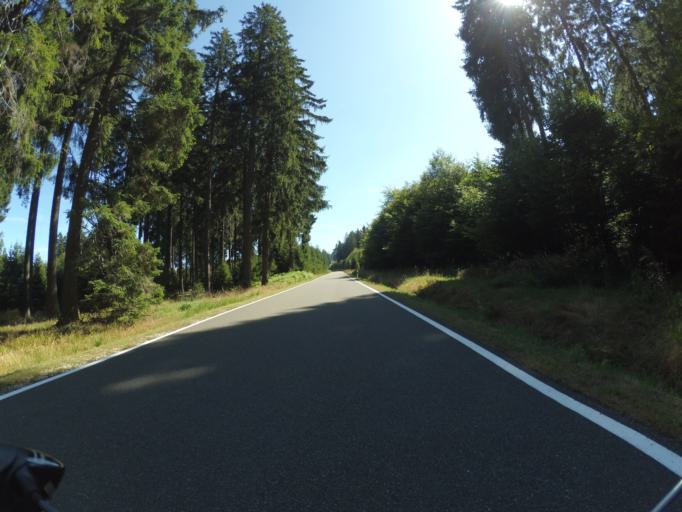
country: DE
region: Rheinland-Pfalz
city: Deuselbach
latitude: 49.7366
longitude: 7.1043
